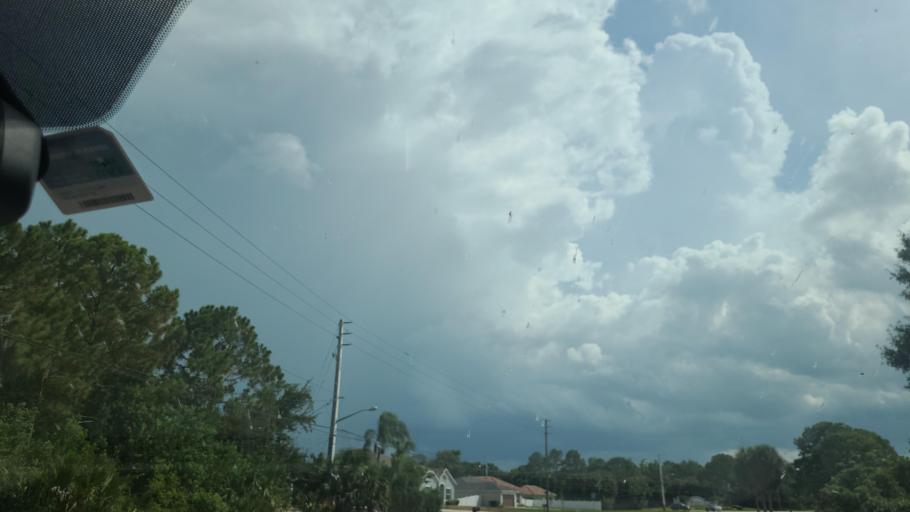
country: US
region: Florida
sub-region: Saint Lucie County
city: Port Saint Lucie
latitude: 27.2471
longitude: -80.3546
